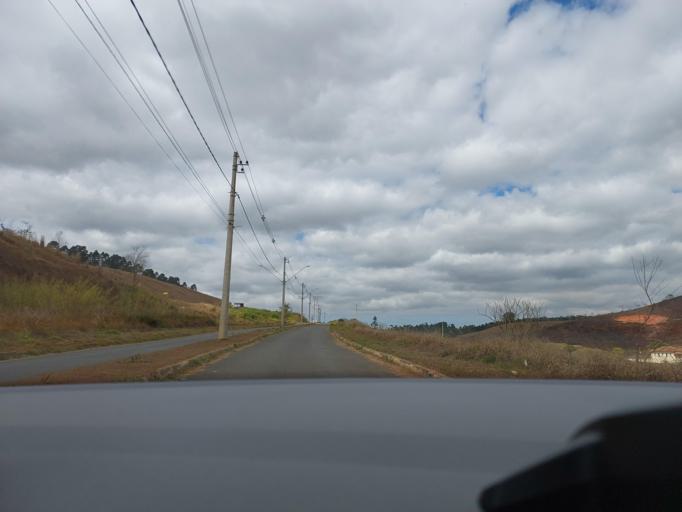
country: BR
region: Minas Gerais
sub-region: Vicosa
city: Vicosa
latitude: -20.7842
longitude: -42.8396
